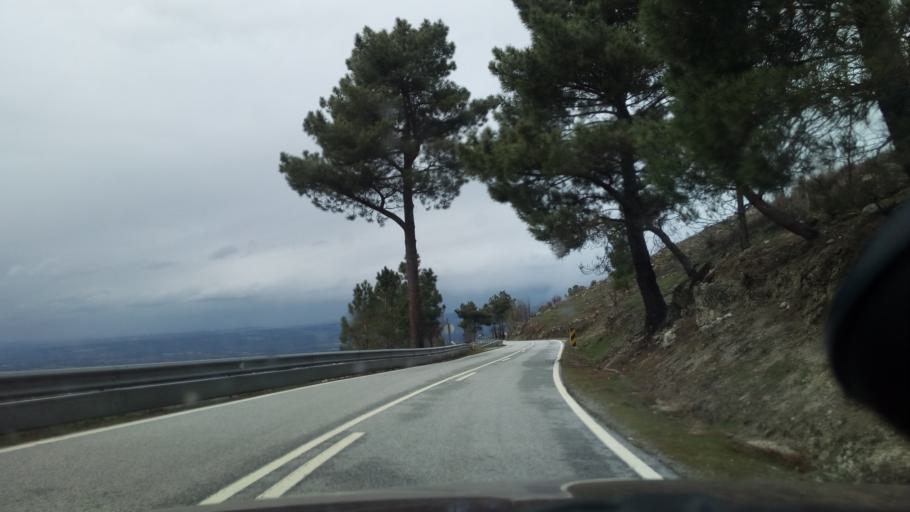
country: PT
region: Guarda
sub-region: Manteigas
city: Manteigas
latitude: 40.4571
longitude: -7.5866
